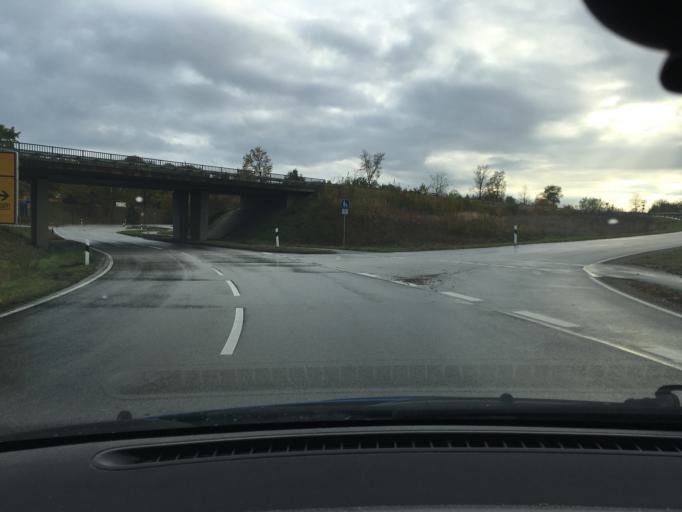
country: DE
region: Schleswig-Holstein
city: Molln
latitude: 53.6427
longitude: 10.6975
